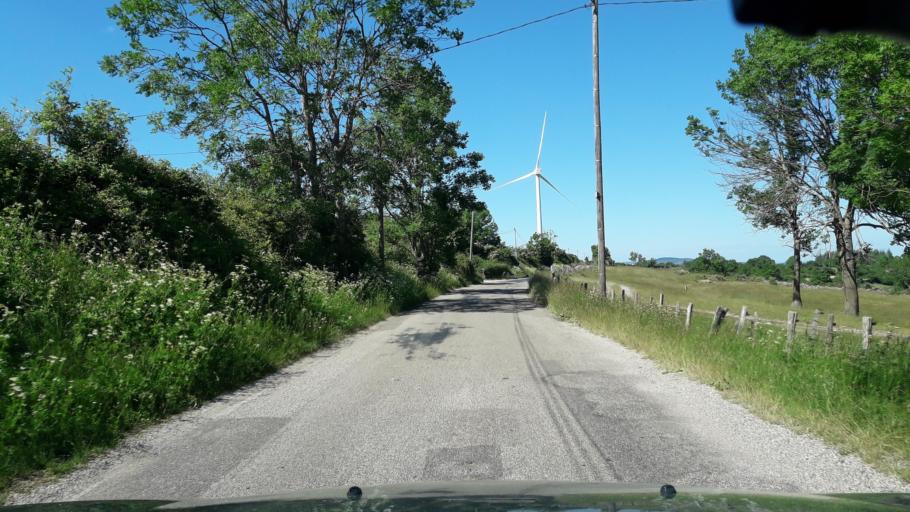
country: FR
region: Rhone-Alpes
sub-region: Departement de l'Ardeche
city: Saint-Priest
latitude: 44.6817
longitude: 4.5590
